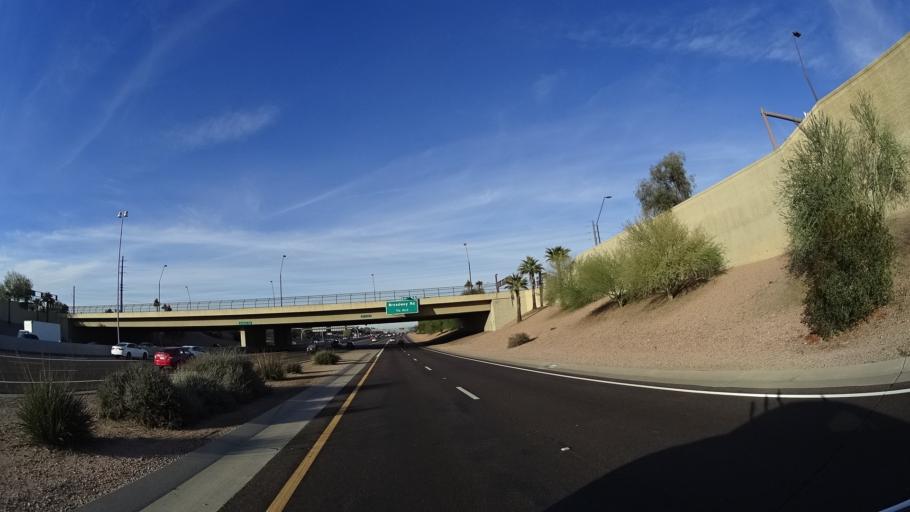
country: US
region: Arizona
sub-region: Maricopa County
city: Tempe
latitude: 33.3919
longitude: -111.8909
